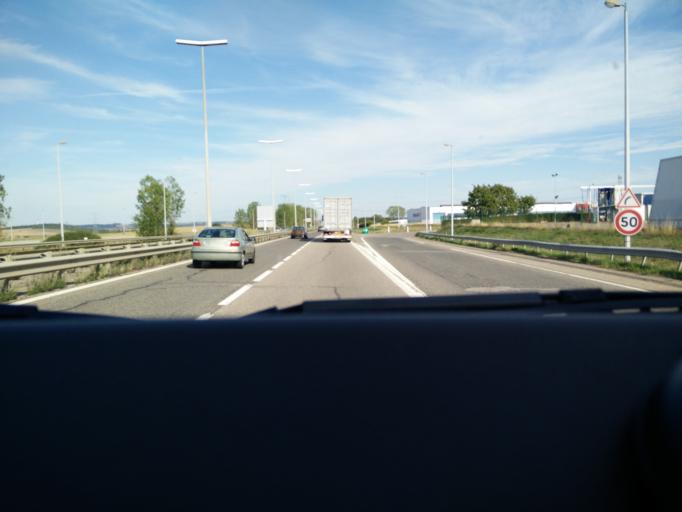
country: FR
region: Lorraine
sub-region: Departement de Meurthe-et-Moselle
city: Fleville-devant-Nancy
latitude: 48.6182
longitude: 6.2081
